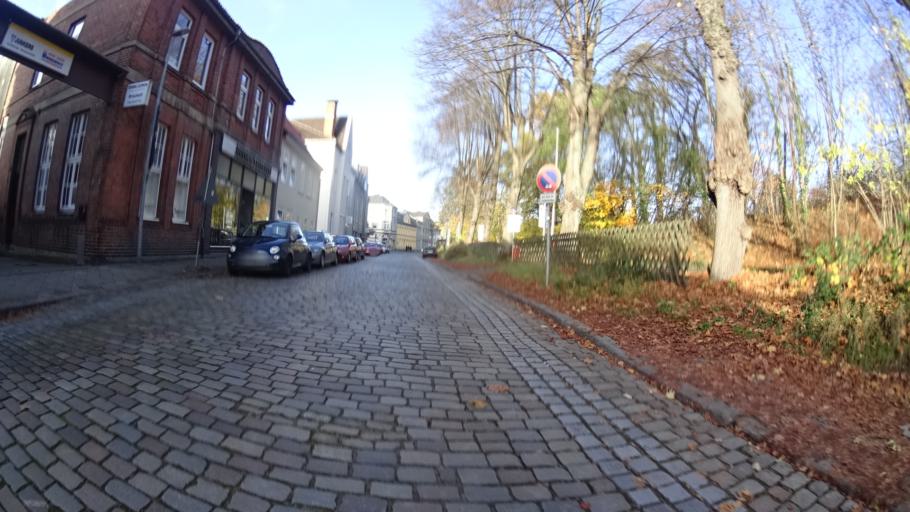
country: DE
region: Lower Saxony
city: Lueneburg
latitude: 53.2502
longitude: 10.4179
